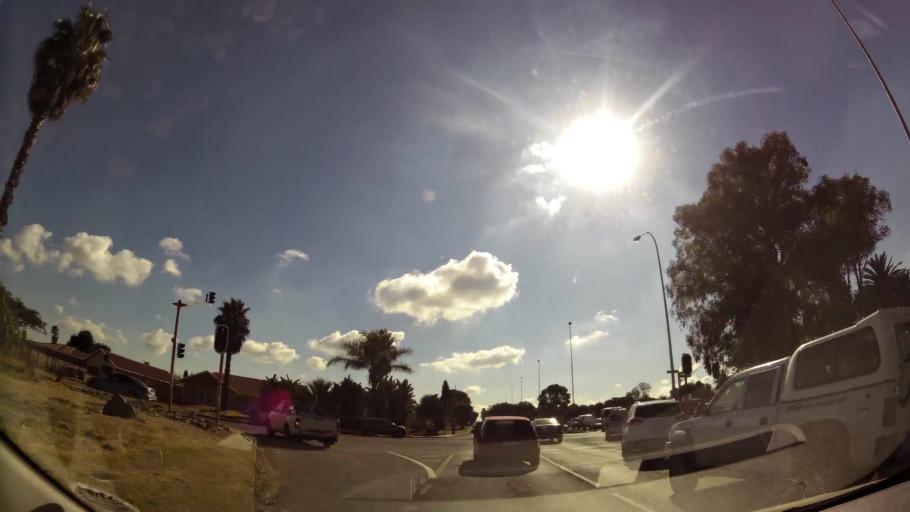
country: ZA
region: Gauteng
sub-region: City of Johannesburg Metropolitan Municipality
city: Roodepoort
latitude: -26.1326
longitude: 27.8379
